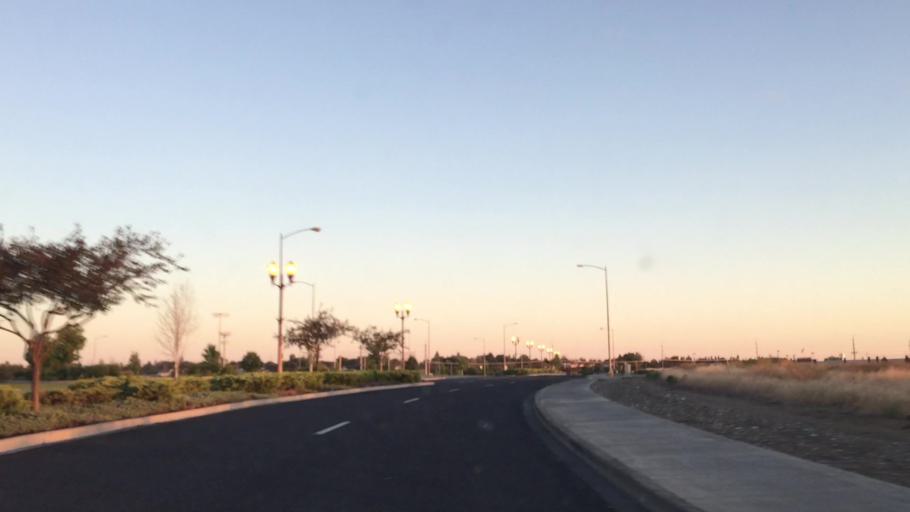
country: US
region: Washington
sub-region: Grant County
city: Moses Lake
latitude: 47.1434
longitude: -119.2883
